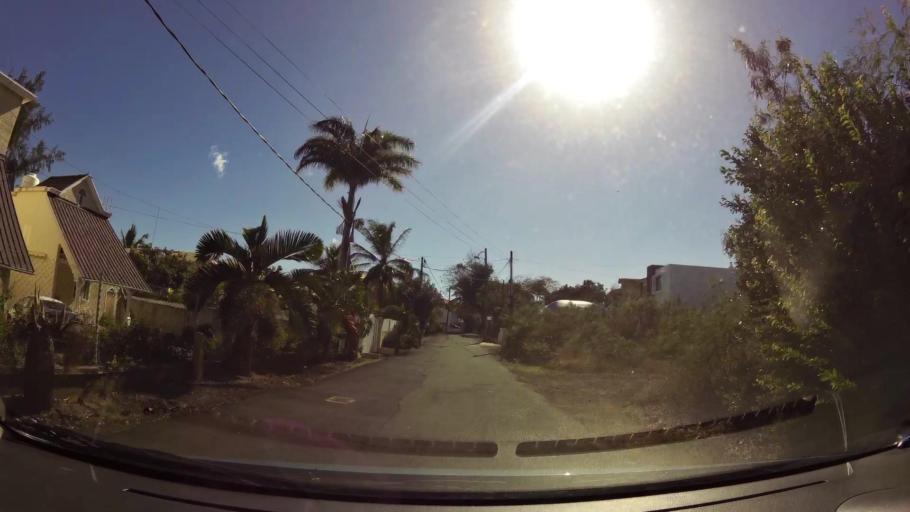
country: MU
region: Black River
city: Flic en Flac
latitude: -20.2651
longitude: 57.3763
